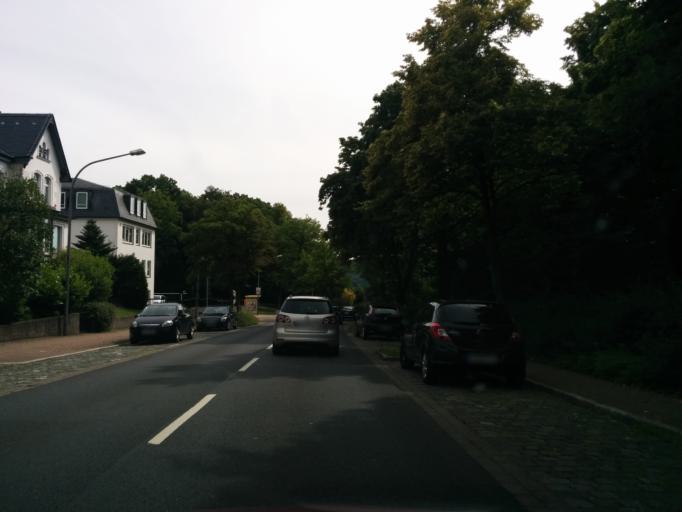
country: DE
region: Lower Saxony
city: Goslar
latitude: 51.9110
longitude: 10.4303
